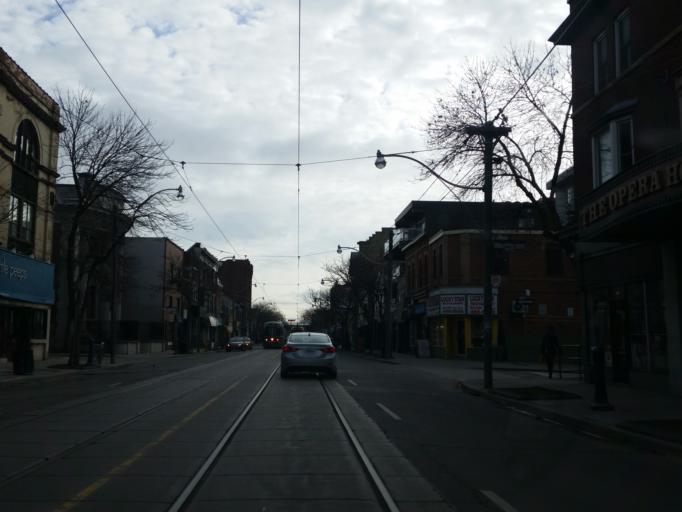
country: CA
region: Ontario
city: Toronto
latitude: 43.6590
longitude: -79.3489
